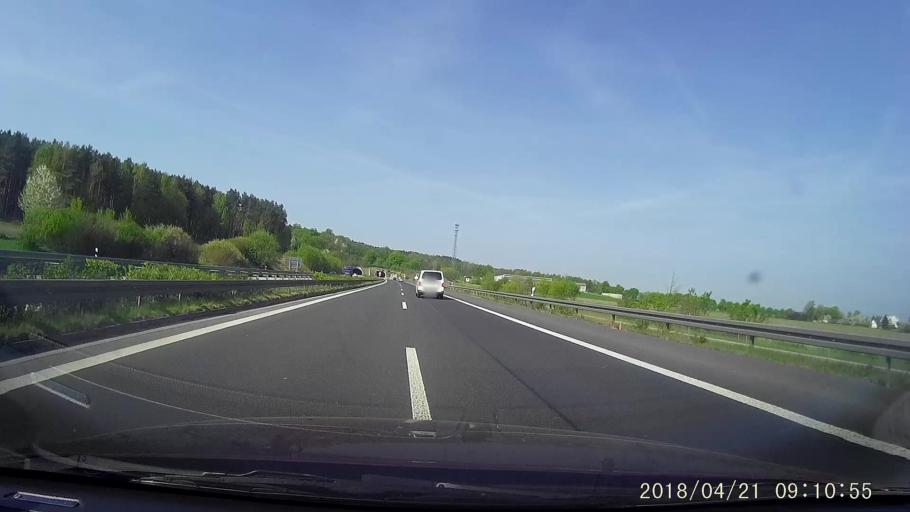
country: DE
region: Saxony
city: Kodersdorf
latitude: 51.2200
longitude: 14.8656
